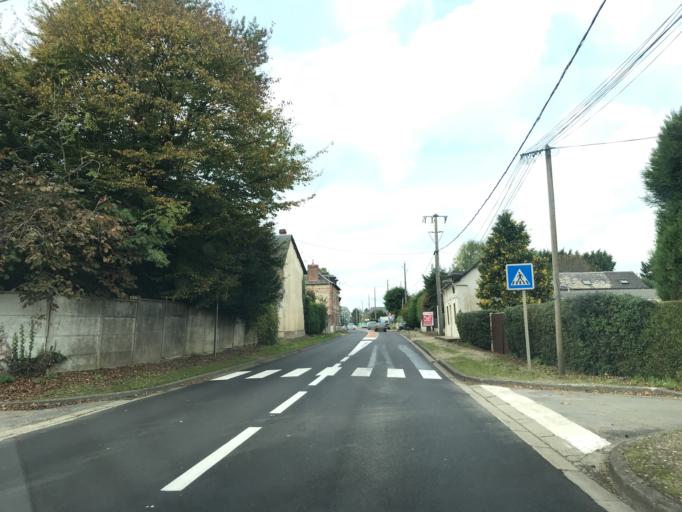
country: FR
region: Haute-Normandie
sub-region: Departement de l'Eure
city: Fleury-sur-Andelle
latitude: 49.3435
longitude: 1.3690
